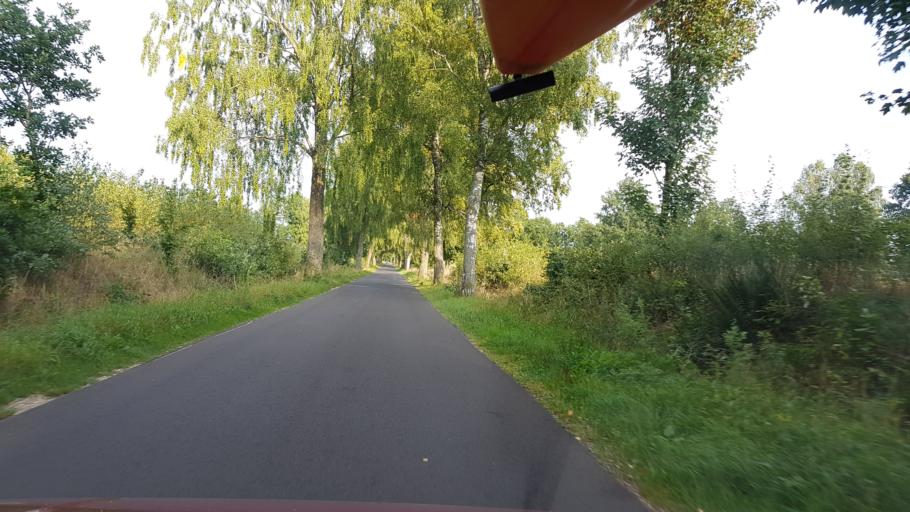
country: PL
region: Pomeranian Voivodeship
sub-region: Powiat bytowski
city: Miastko
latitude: 54.0205
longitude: 16.8637
